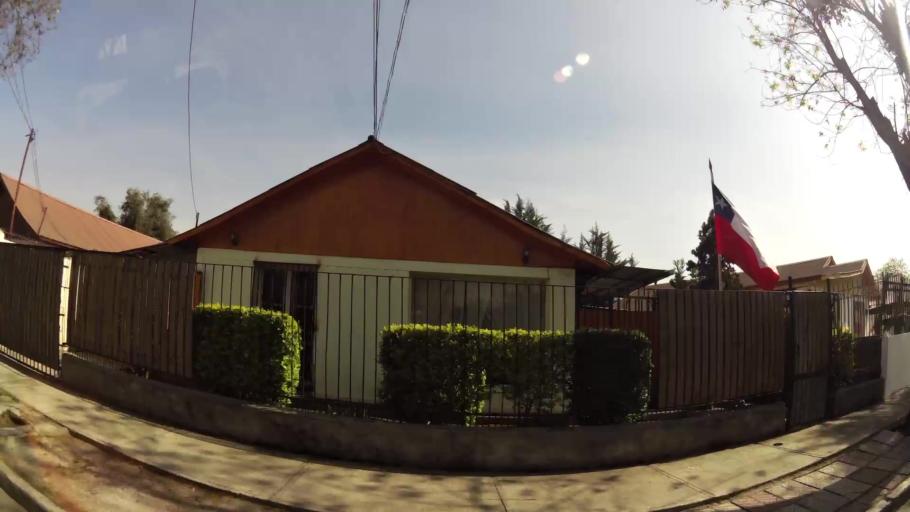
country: CL
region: Santiago Metropolitan
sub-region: Provincia de Santiago
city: Villa Presidente Frei, Nunoa, Santiago, Chile
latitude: -33.4922
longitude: -70.5925
